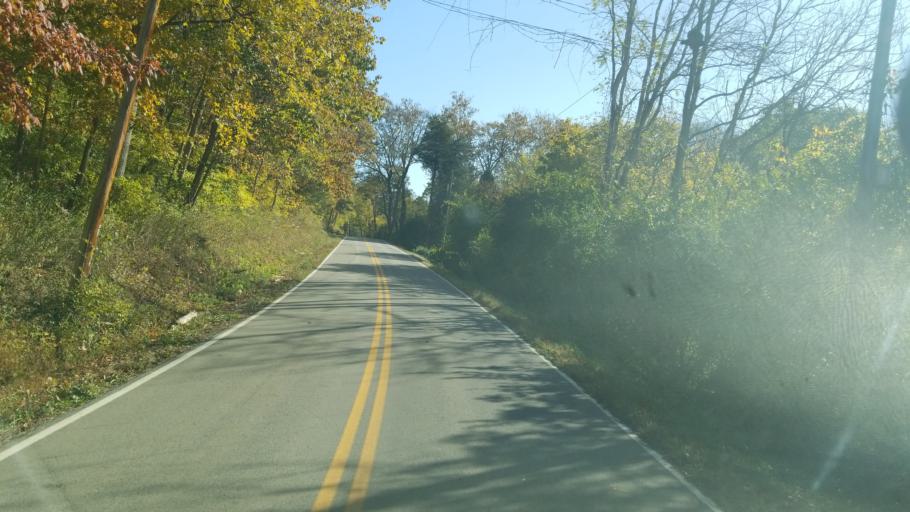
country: US
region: Ohio
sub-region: Warren County
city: Morrow
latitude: 39.3609
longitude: -84.1199
